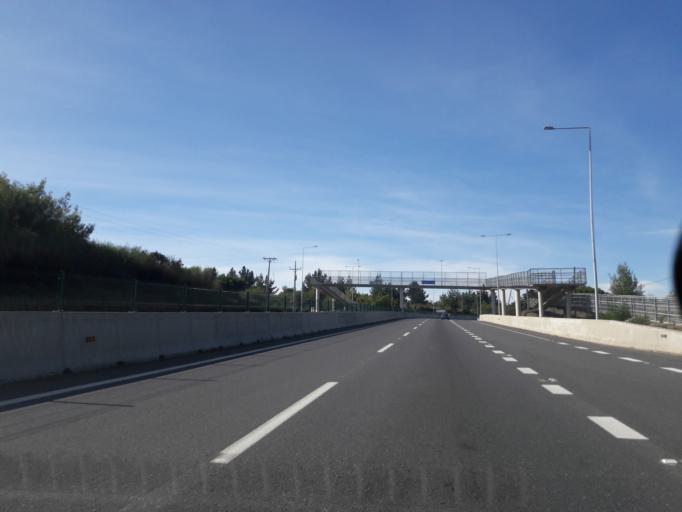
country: CL
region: Biobio
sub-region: Provincia de Biobio
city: Yumbel
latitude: -36.9741
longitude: -72.6569
